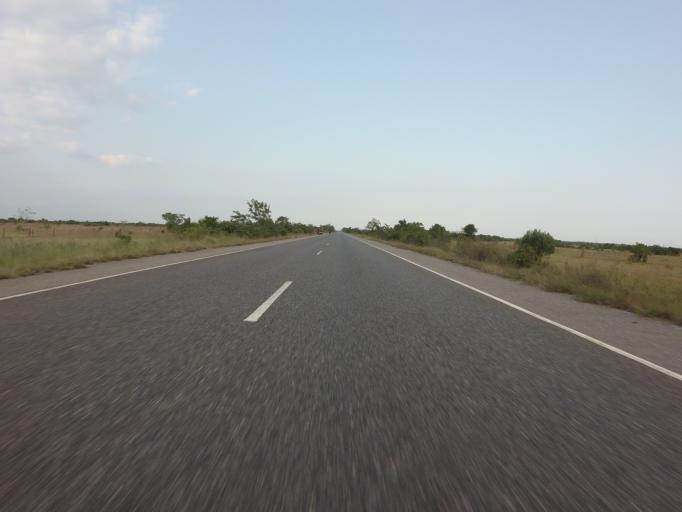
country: GH
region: Volta
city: Anloga
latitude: 6.0824
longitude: 0.5679
